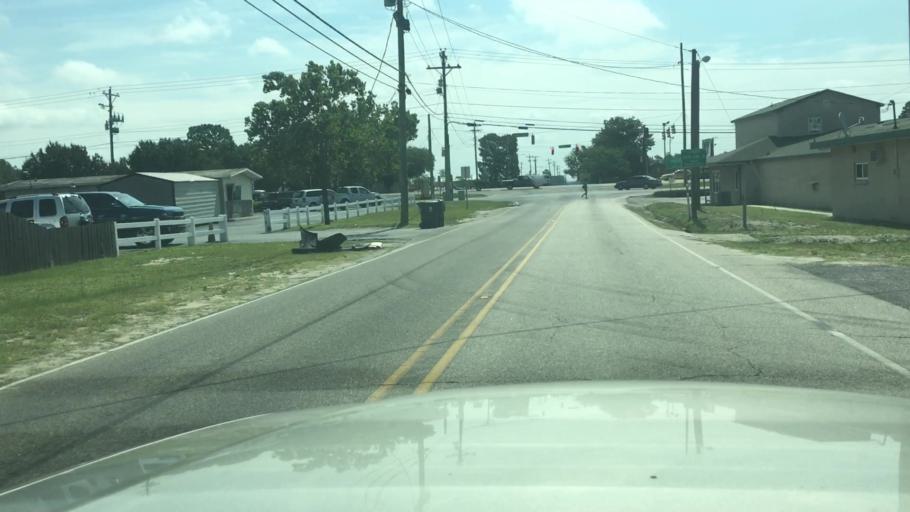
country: US
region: North Carolina
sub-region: Cumberland County
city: Fayetteville
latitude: 35.0134
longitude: -78.8984
